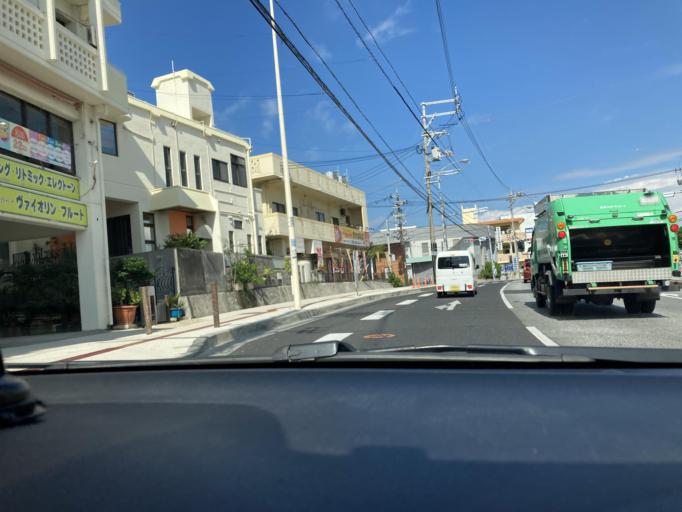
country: JP
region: Okinawa
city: Naha-shi
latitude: 26.2363
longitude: 127.6975
